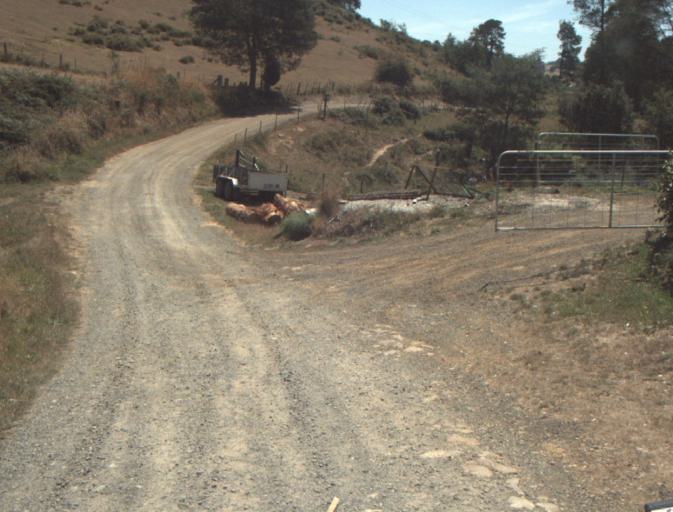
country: AU
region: Tasmania
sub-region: Launceston
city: Mayfield
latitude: -41.2707
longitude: 147.1330
